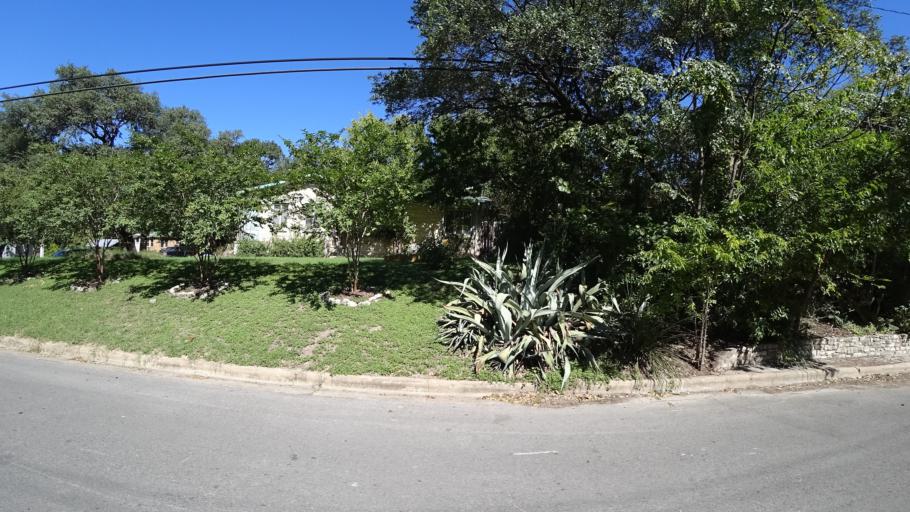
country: US
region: Texas
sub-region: Travis County
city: Austin
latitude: 30.2451
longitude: -97.7426
